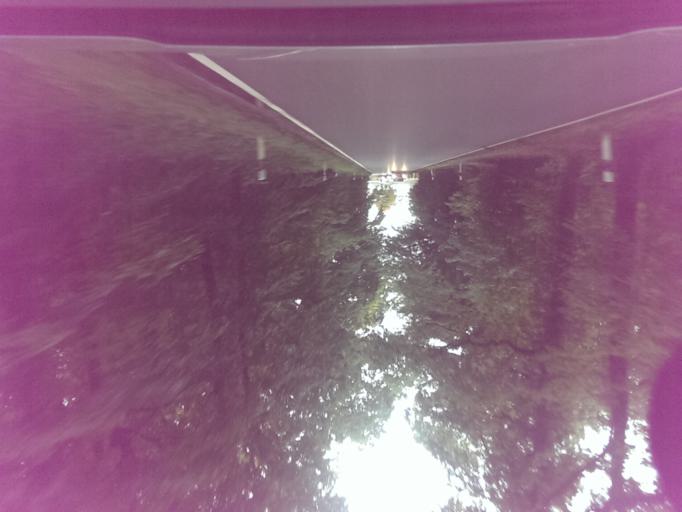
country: DE
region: Lower Saxony
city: Seelze
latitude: 52.3846
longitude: 9.5784
